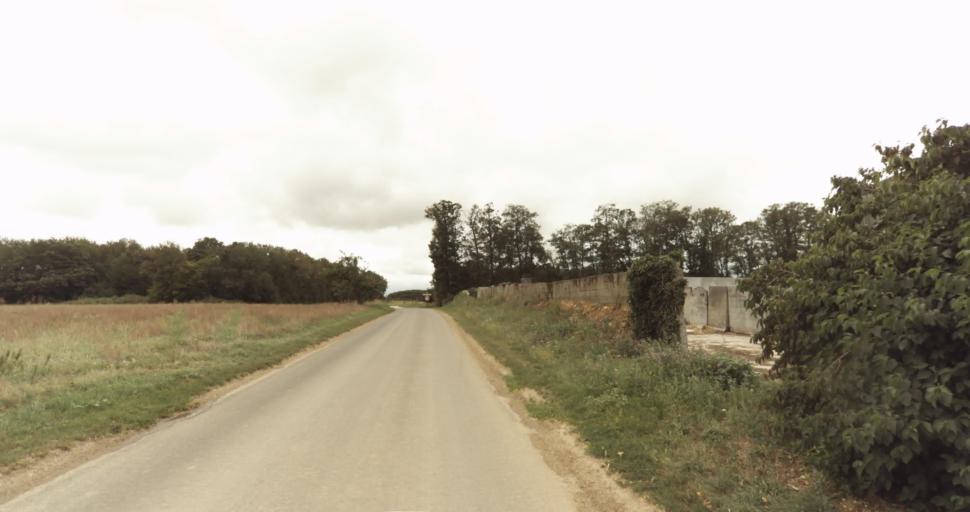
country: FR
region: Haute-Normandie
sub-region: Departement de l'Eure
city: Evreux
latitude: 48.9306
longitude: 1.2021
